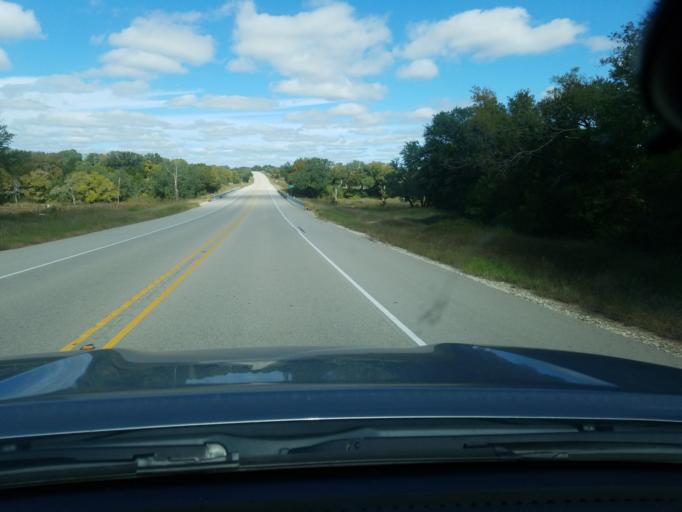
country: US
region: Texas
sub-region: Hamilton County
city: Hamilton
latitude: 31.5809
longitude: -98.1572
